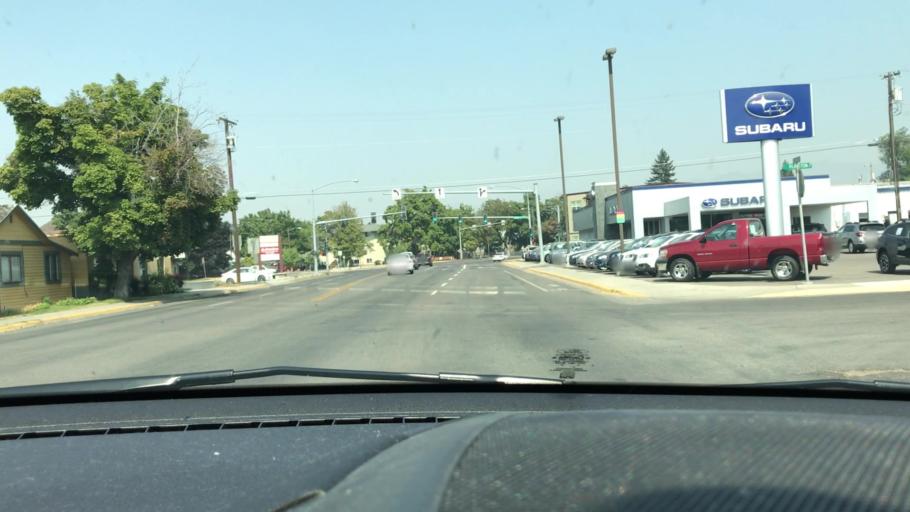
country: US
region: Montana
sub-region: Missoula County
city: Missoula
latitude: 46.8549
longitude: -114.0128
